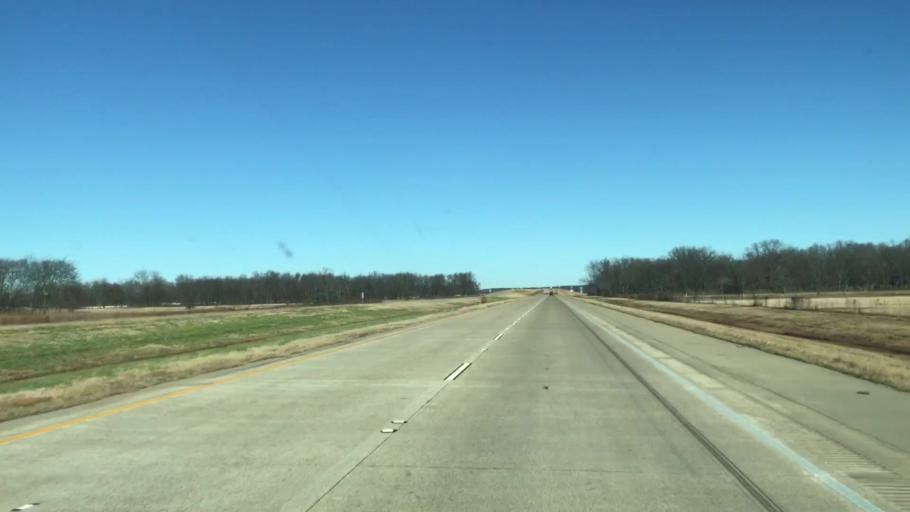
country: US
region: Louisiana
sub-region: Caddo Parish
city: Oil City
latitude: 32.7376
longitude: -93.8762
